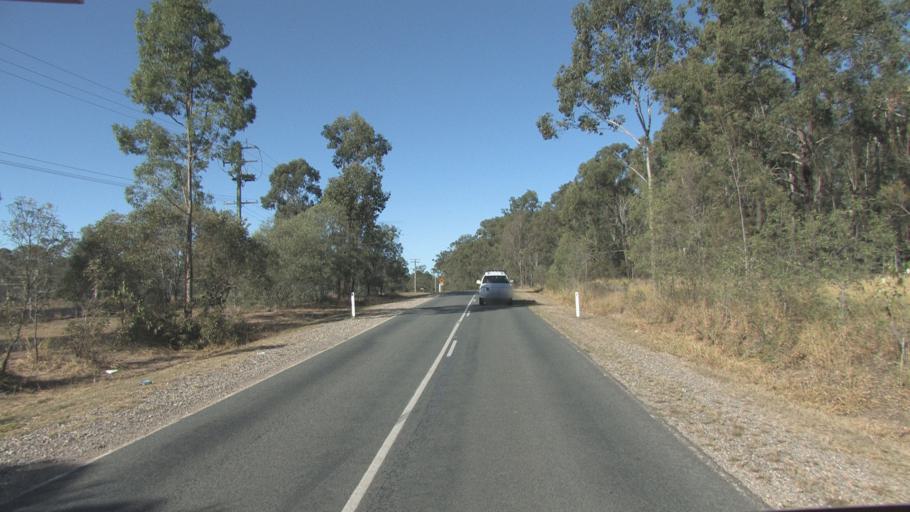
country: AU
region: Queensland
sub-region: Logan
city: North Maclean
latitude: -27.7911
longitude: 153.0363
